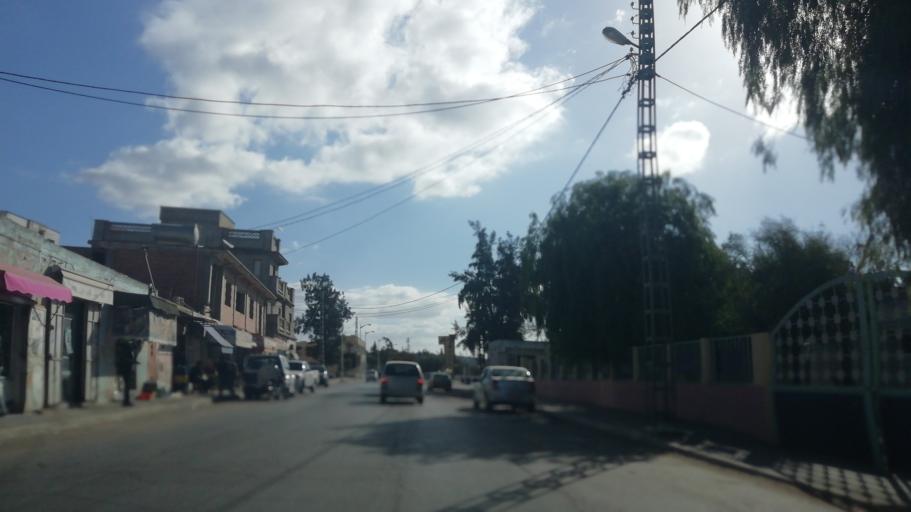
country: DZ
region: Mostaganem
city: Mostaganem
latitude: 35.9923
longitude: 0.2931
